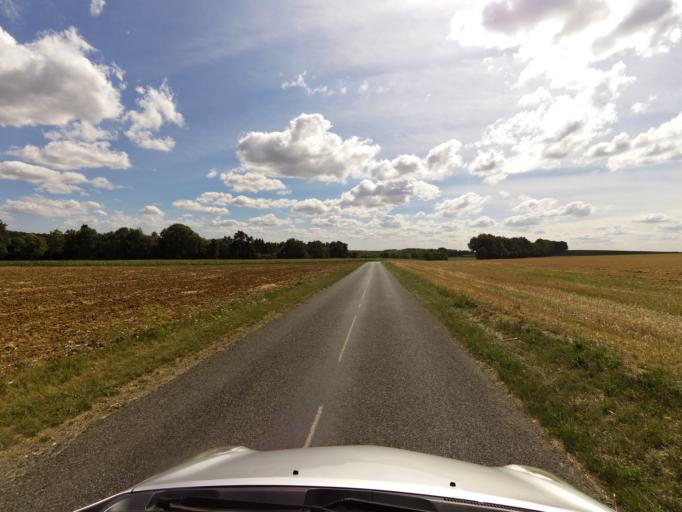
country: FR
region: Picardie
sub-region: Departement de l'Aisne
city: Bruyeres-et-Montberault
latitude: 49.4961
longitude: 3.6242
